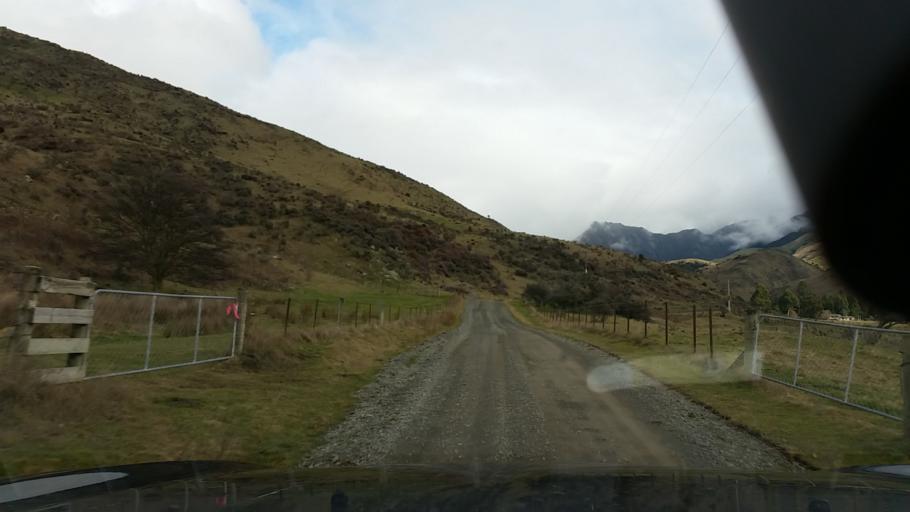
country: NZ
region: Tasman
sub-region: Tasman District
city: Richmond
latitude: -41.7334
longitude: 173.4331
